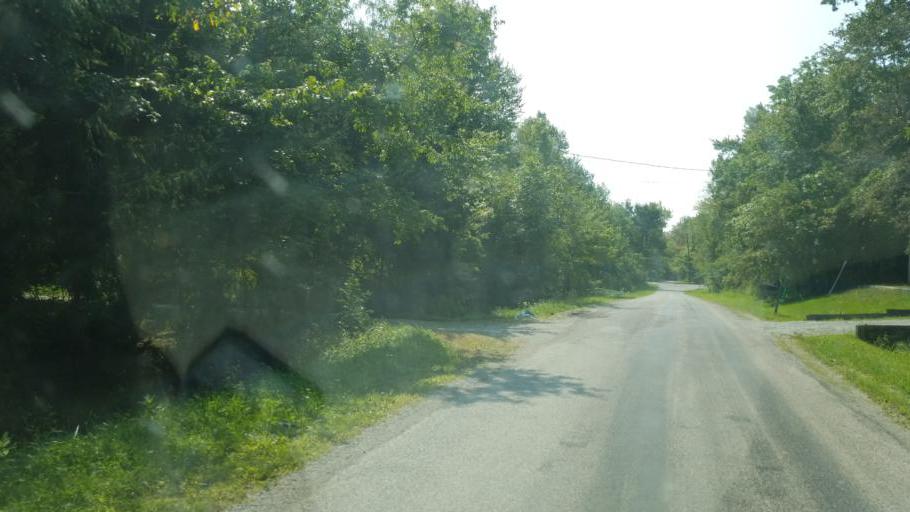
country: US
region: Ohio
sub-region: Lake County
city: Madison
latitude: 41.6351
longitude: -81.0028
